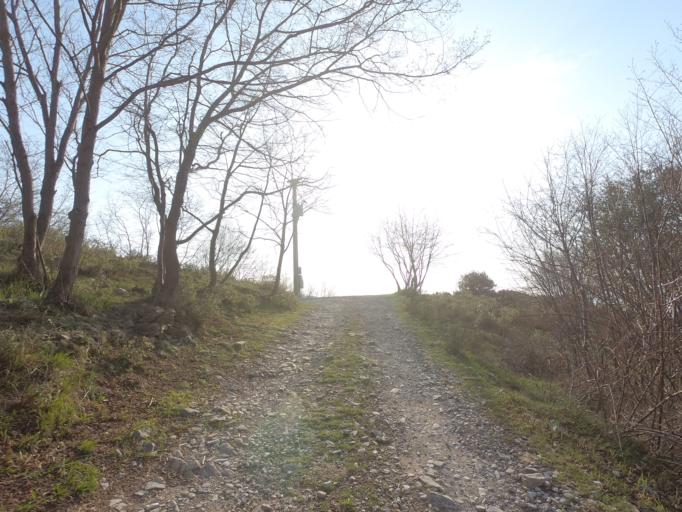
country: IT
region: Liguria
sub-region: Provincia di Savona
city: Balestrino
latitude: 44.1093
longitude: 8.1622
